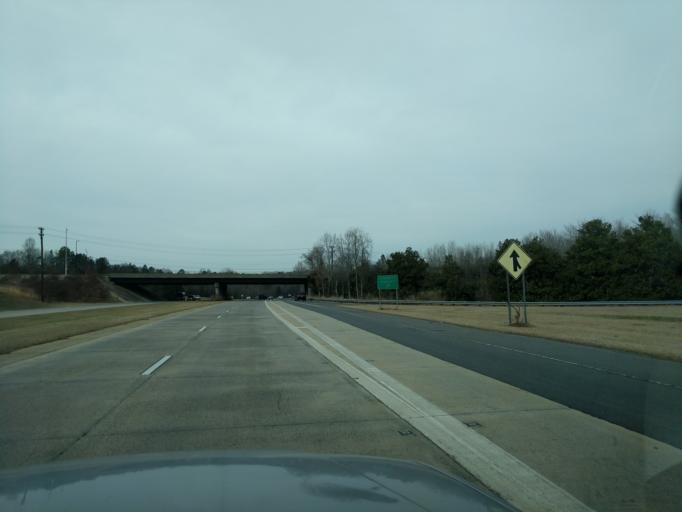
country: US
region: North Carolina
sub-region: Mecklenburg County
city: Charlotte
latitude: 35.1929
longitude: -80.9168
